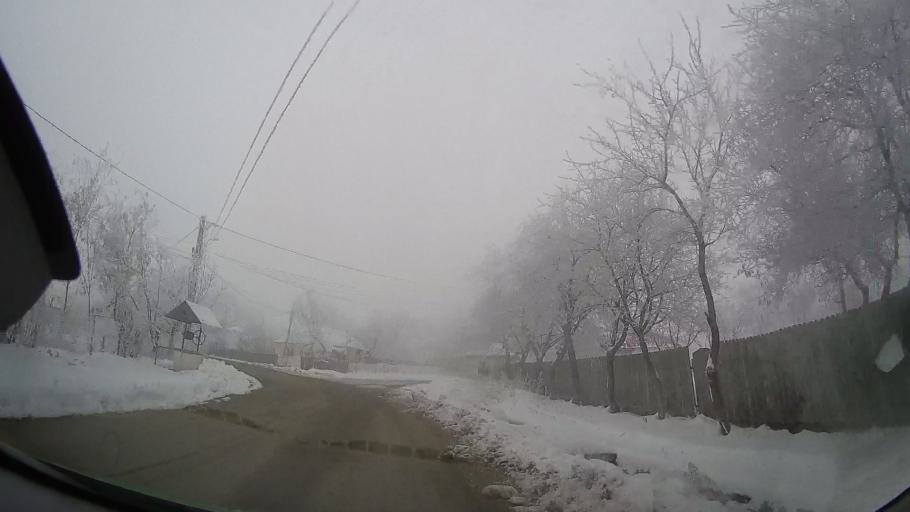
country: RO
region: Iasi
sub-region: Comuna Tansa
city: Suhulet
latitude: 46.8988
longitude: 27.2626
